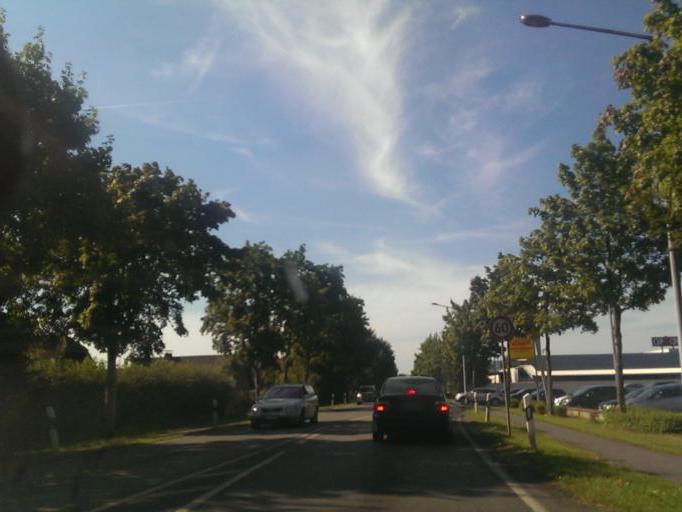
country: DE
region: North Rhine-Westphalia
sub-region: Regierungsbezirk Detmold
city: Hovelhof
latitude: 51.8152
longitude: 8.6637
